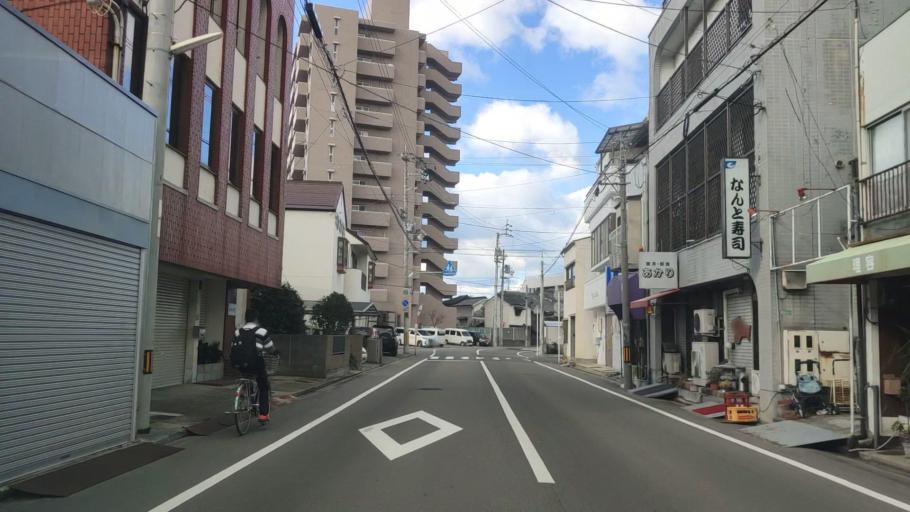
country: JP
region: Ehime
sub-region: Shikoku-chuo Shi
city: Matsuyama
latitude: 33.8646
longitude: 132.7147
